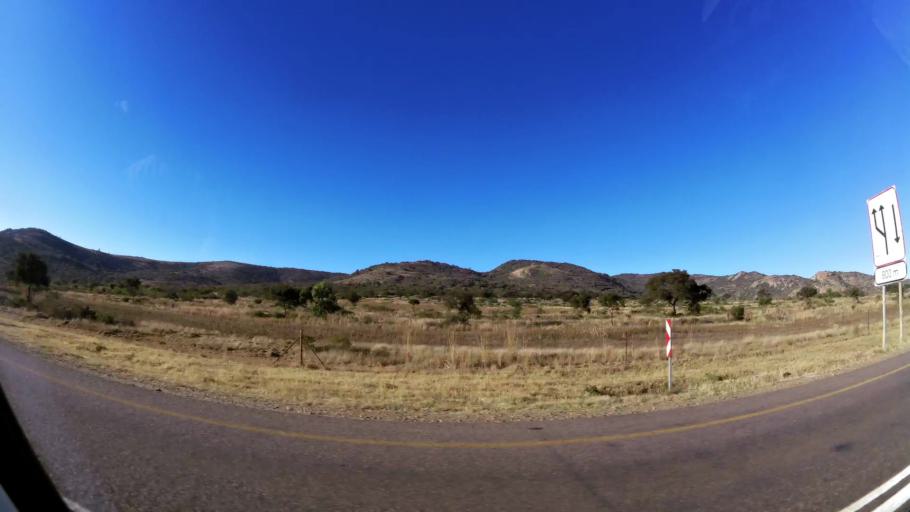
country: ZA
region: Limpopo
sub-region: Capricorn District Municipality
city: Mankoeng
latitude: -23.9243
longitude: 29.8744
